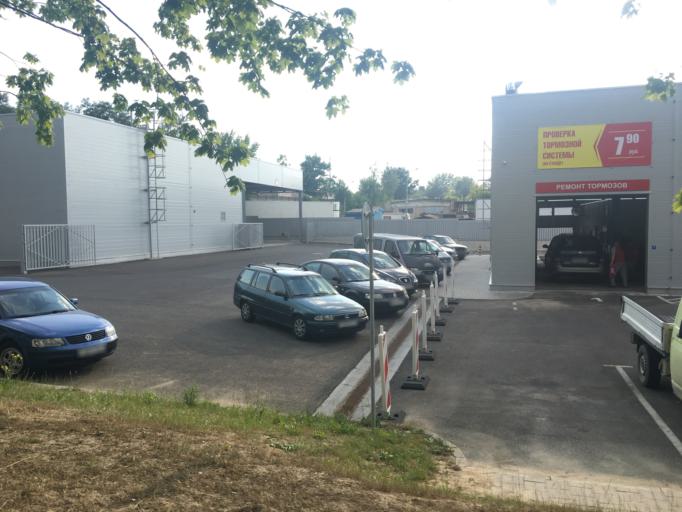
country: BY
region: Grodnenskaya
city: Hrodna
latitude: 53.6578
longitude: 23.8304
